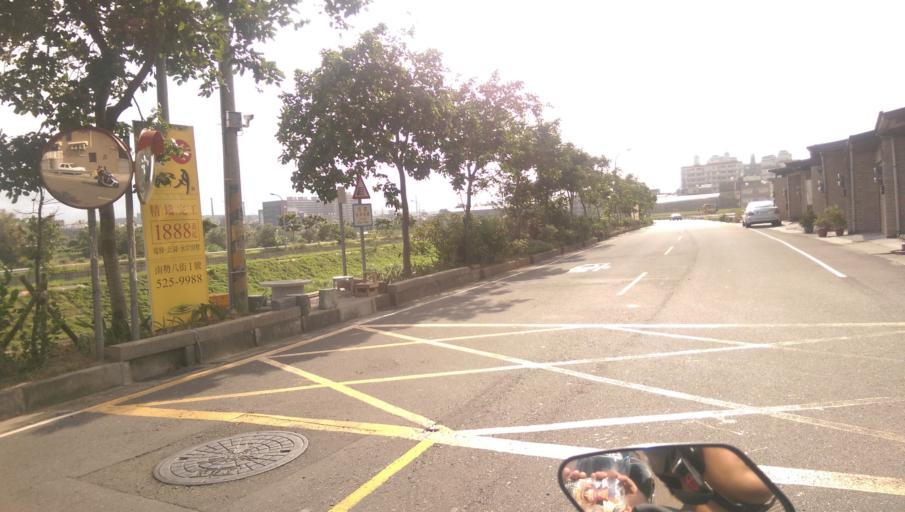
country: TW
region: Taiwan
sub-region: Hsinchu
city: Hsinchu
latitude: 24.8046
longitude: 120.9429
